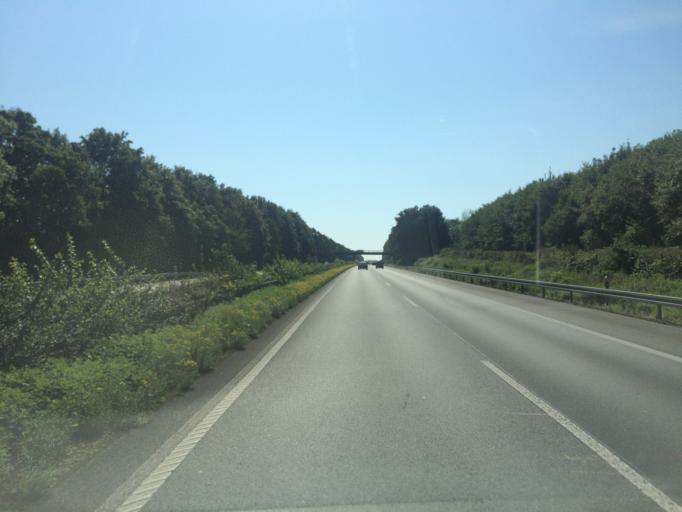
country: DE
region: North Rhine-Westphalia
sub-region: Regierungsbezirk Munster
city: Ascheberg
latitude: 51.7415
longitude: 7.6498
